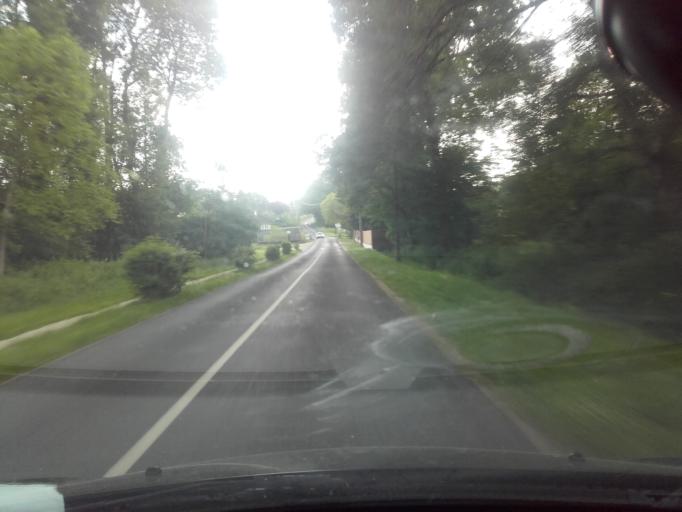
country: FR
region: Centre
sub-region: Departement du Loir-et-Cher
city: Chouzy-sur-Cisse
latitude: 47.5602
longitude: 1.2105
